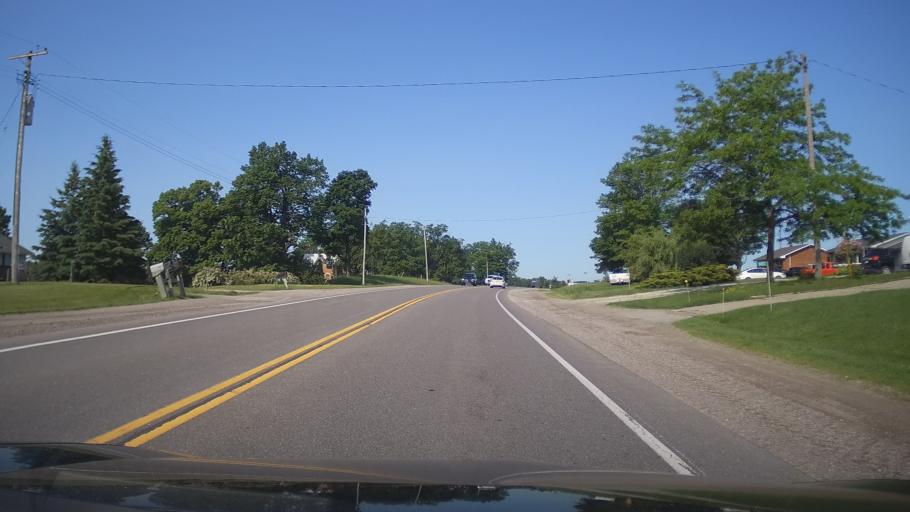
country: CA
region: Ontario
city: Omemee
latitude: 44.3470
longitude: -78.8109
